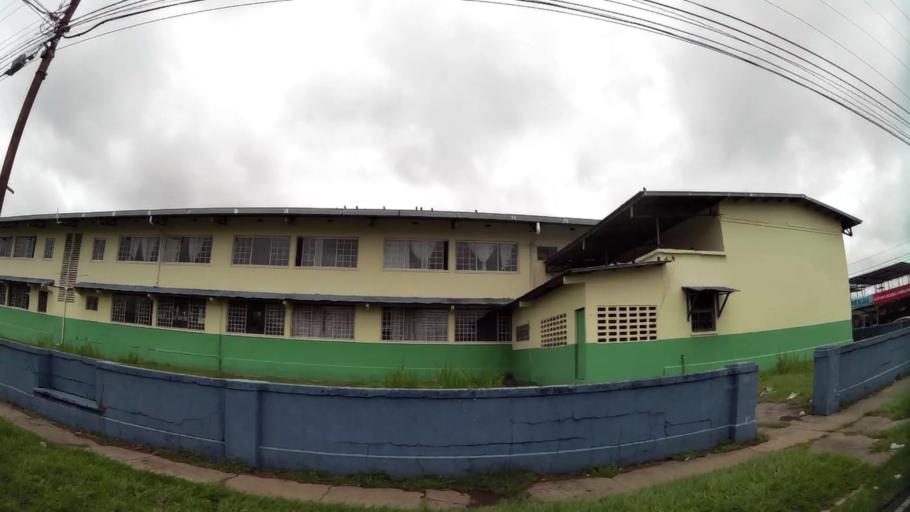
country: PA
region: Chiriqui
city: David
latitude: 8.4269
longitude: -82.4282
